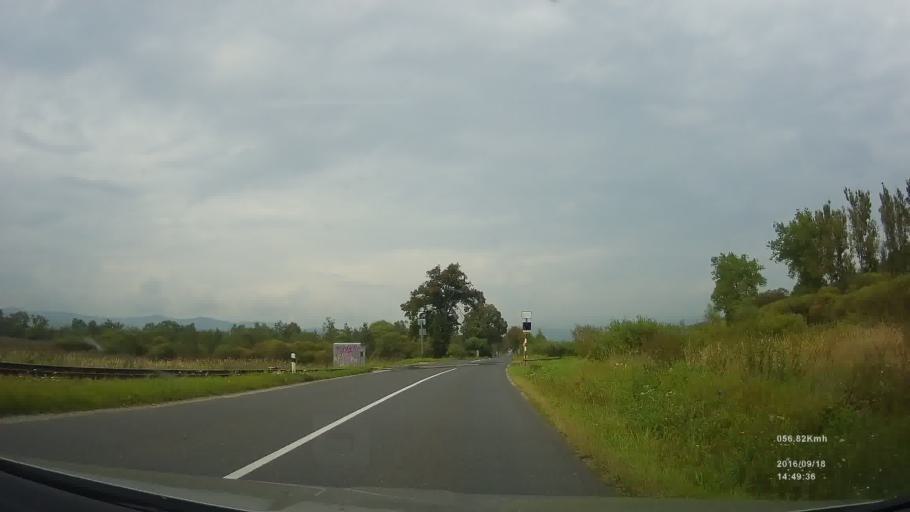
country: SK
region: Presovsky
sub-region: Okres Presov
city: Levoca
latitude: 48.9867
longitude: 20.5800
